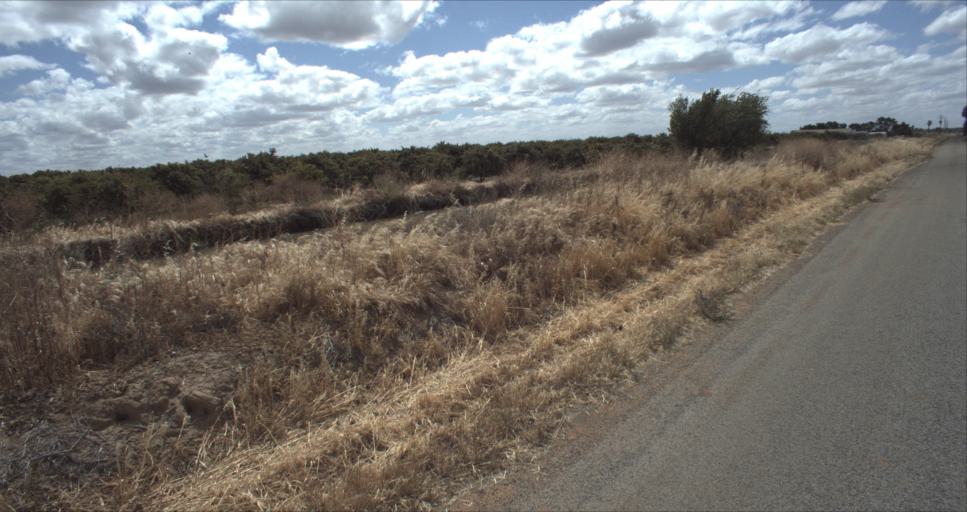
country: AU
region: New South Wales
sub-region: Leeton
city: Leeton
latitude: -34.5874
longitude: 146.3911
